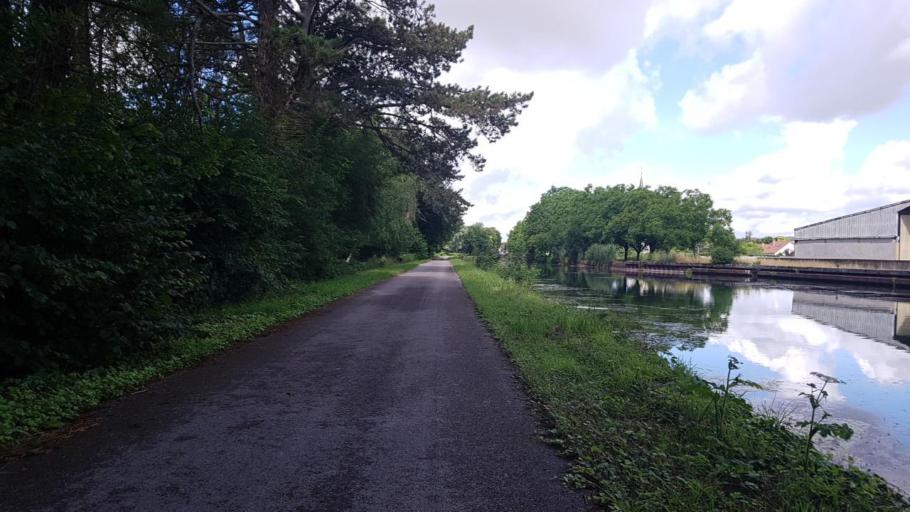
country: FR
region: Champagne-Ardenne
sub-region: Departement de la Marne
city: Tours-sur-Marne
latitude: 49.0456
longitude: 4.1296
